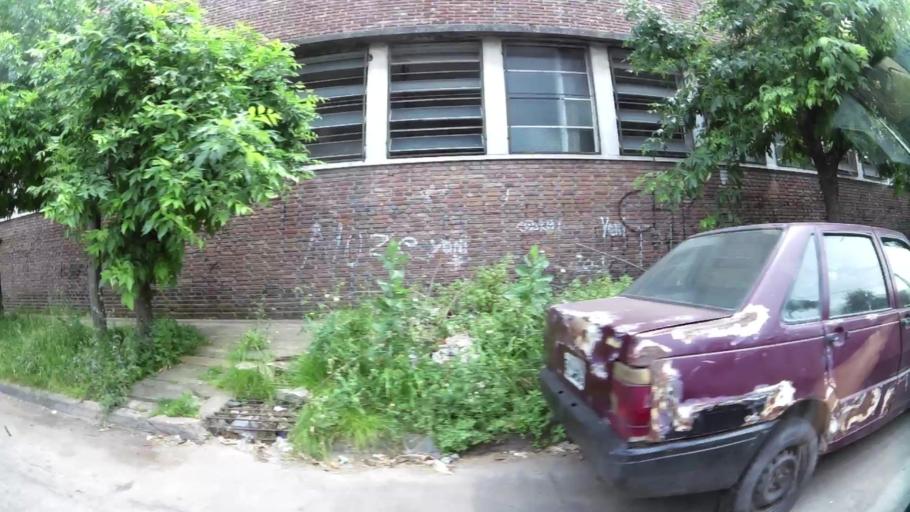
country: AR
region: Buenos Aires
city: San Justo
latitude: -34.6816
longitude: -58.5218
